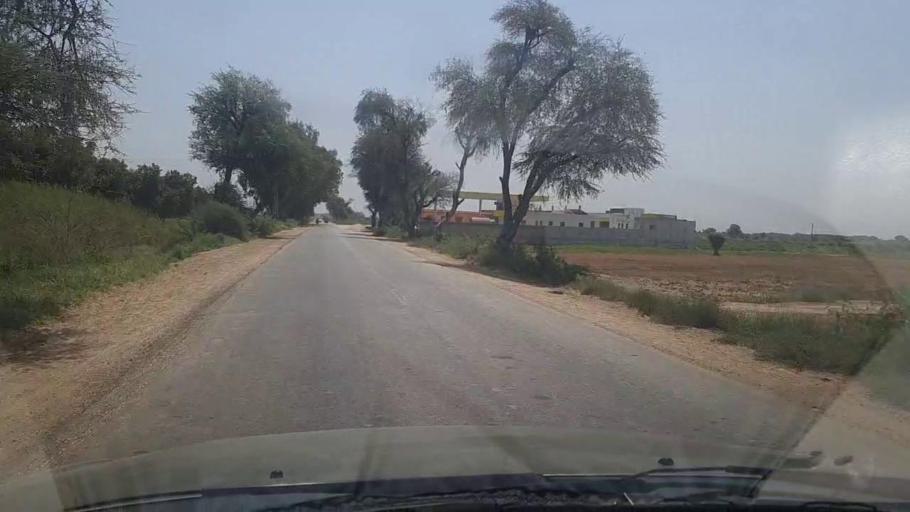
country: PK
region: Sindh
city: Tando Jam
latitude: 25.3662
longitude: 68.4829
